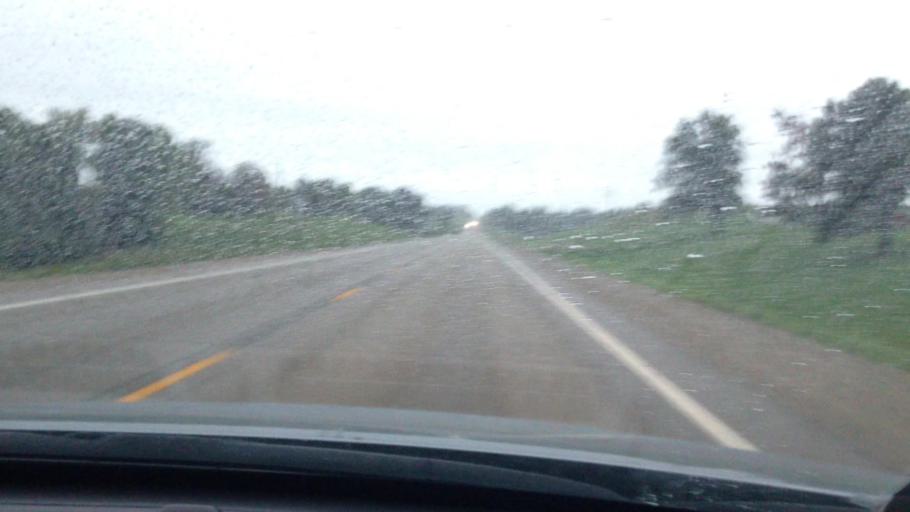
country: US
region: Kansas
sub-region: Brown County
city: Hiawatha
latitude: 39.8310
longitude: -95.5270
